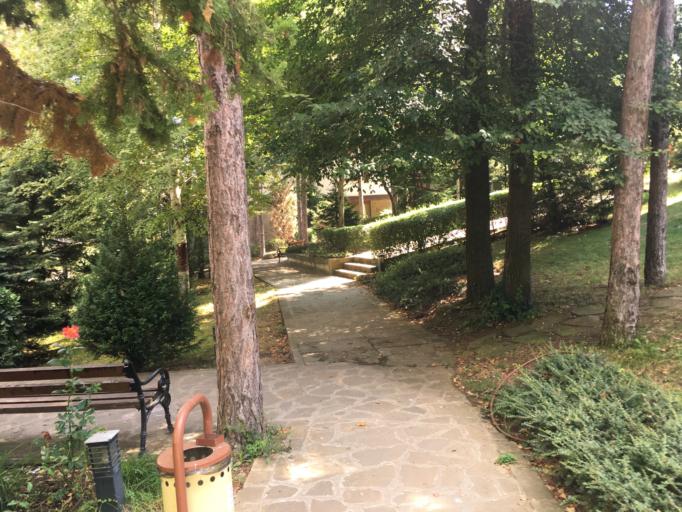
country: BG
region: Burgas
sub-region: Obshtina Sozopol
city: Sozopol
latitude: 42.4120
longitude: 27.6793
